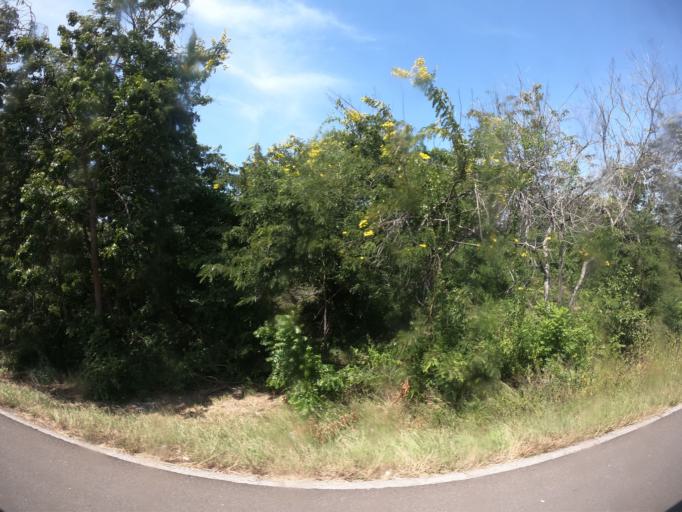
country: TH
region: Nakhon Ratchasima
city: Non Daeng
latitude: 15.4548
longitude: 102.5009
